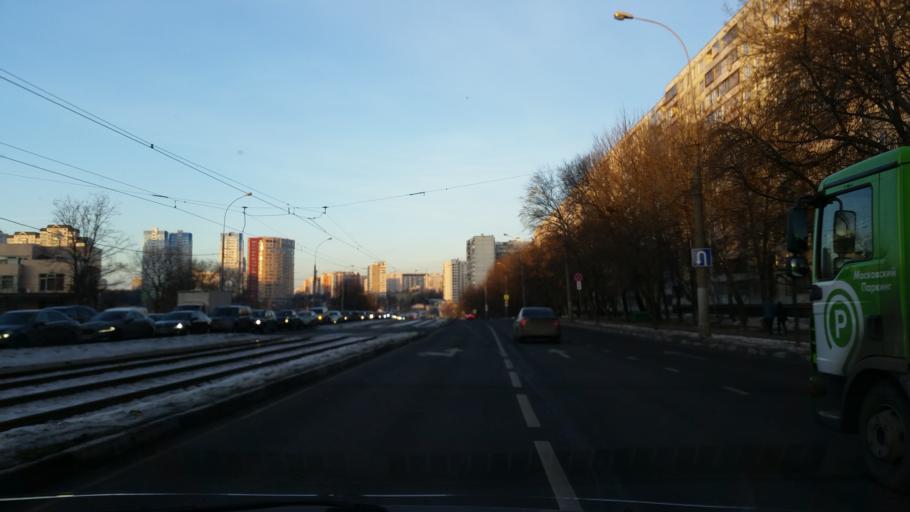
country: RU
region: Moscow
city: Nagornyy
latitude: 55.6352
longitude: 37.6041
